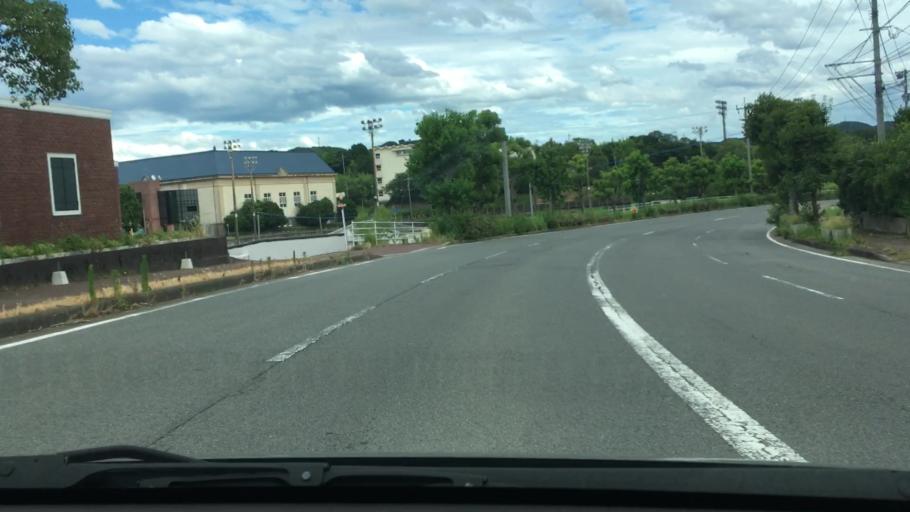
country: JP
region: Nagasaki
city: Sasebo
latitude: 32.9943
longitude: 129.7585
